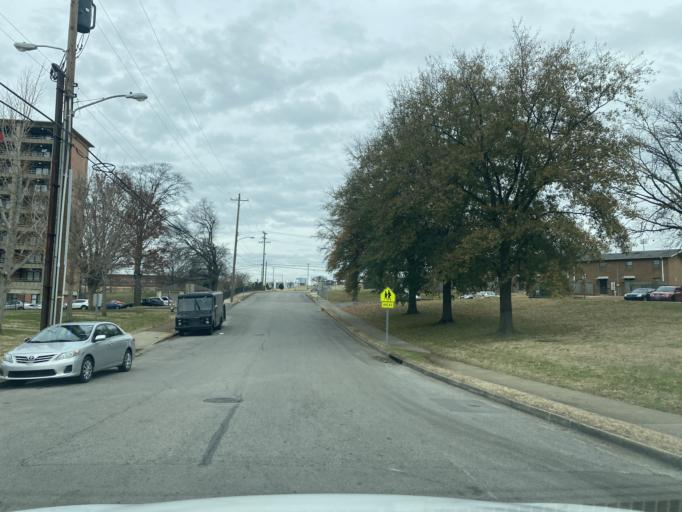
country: US
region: Tennessee
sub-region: Davidson County
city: Nashville
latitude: 36.1411
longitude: -86.7857
